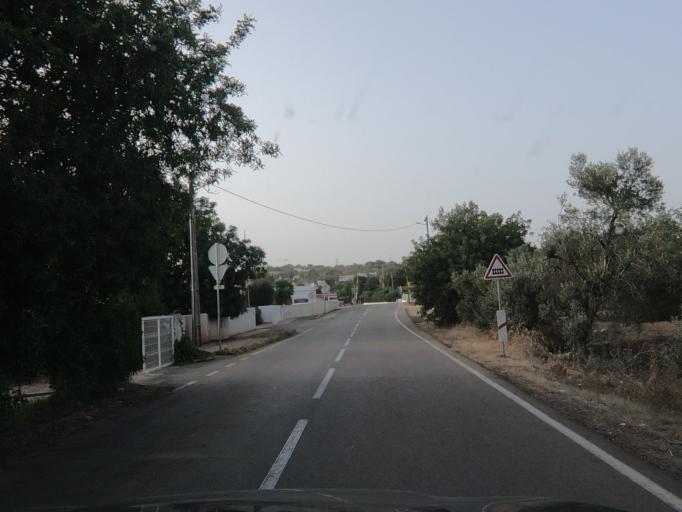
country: PT
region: Faro
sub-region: Loule
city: Vilamoura
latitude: 37.1100
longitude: -8.0885
